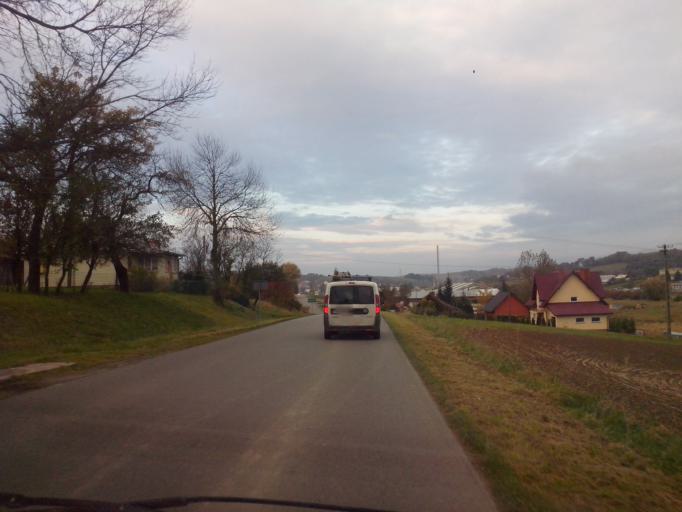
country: PL
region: Subcarpathian Voivodeship
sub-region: Powiat ropczycko-sedziszowski
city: Wielopole Skrzynskie
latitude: 49.9477
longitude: 21.6281
